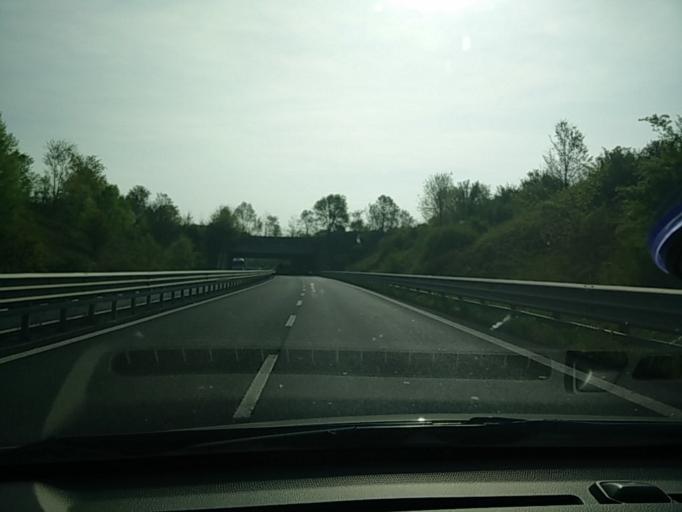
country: IT
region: Friuli Venezia Giulia
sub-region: Provincia di Udine
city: Zugliano-Terenzano-Cargnacco
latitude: 46.0155
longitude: 13.2477
